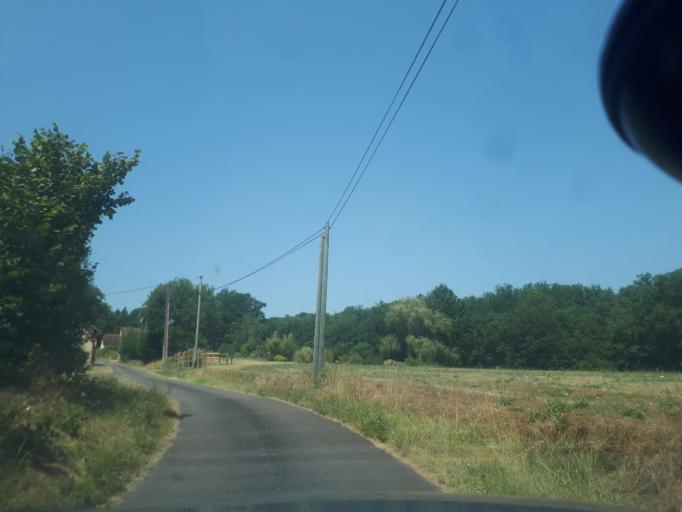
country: FR
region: Midi-Pyrenees
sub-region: Departement du Lot
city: Salviac
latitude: 44.7335
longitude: 1.3117
